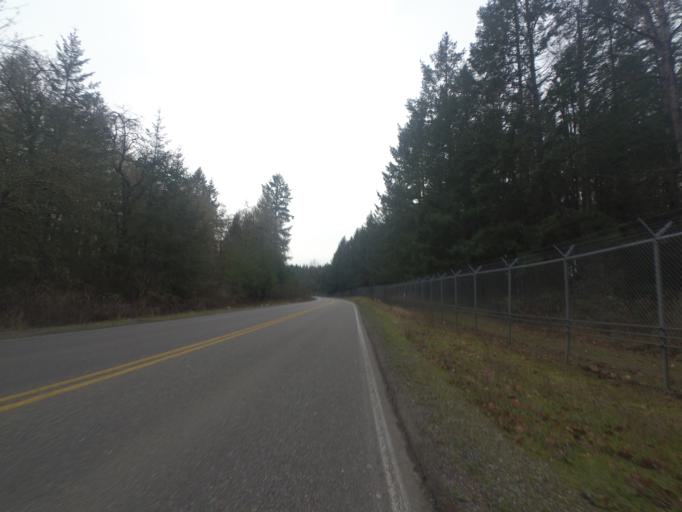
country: US
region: Washington
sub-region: Pierce County
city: McChord Air Force Base
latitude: 47.1197
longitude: -122.5062
